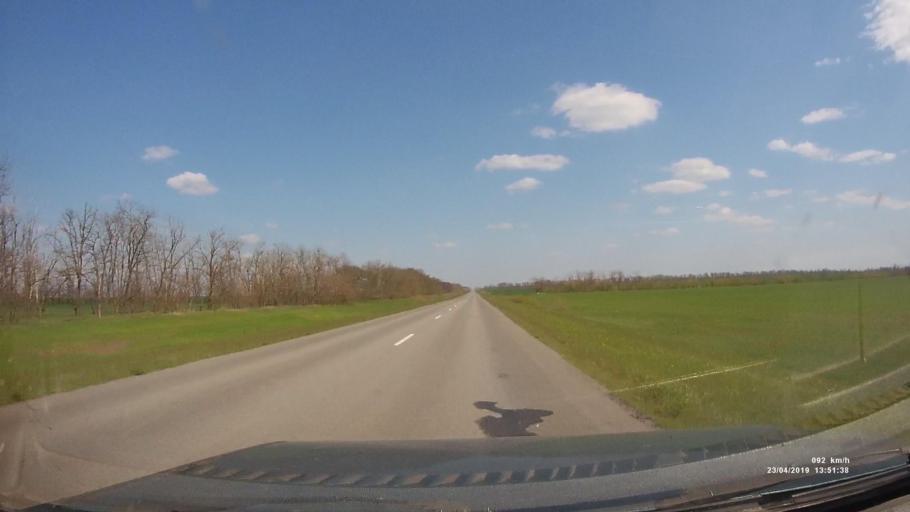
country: RU
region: Kalmykiya
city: Yashalta
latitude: 46.5995
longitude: 42.9378
